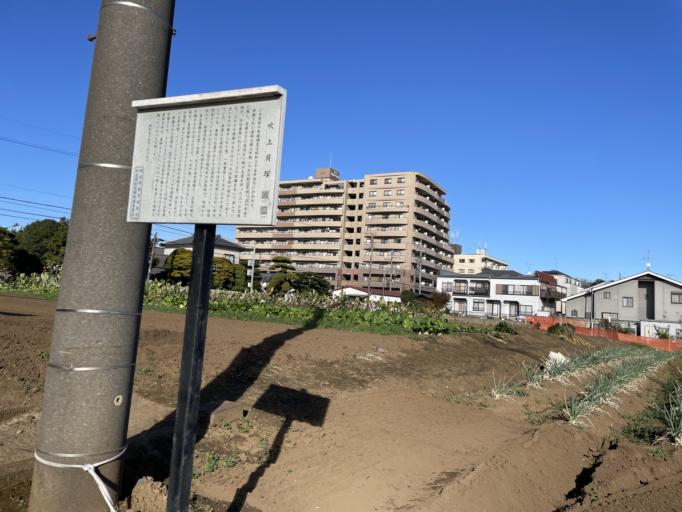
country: JP
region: Saitama
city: Wako
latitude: 35.7907
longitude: 139.6315
